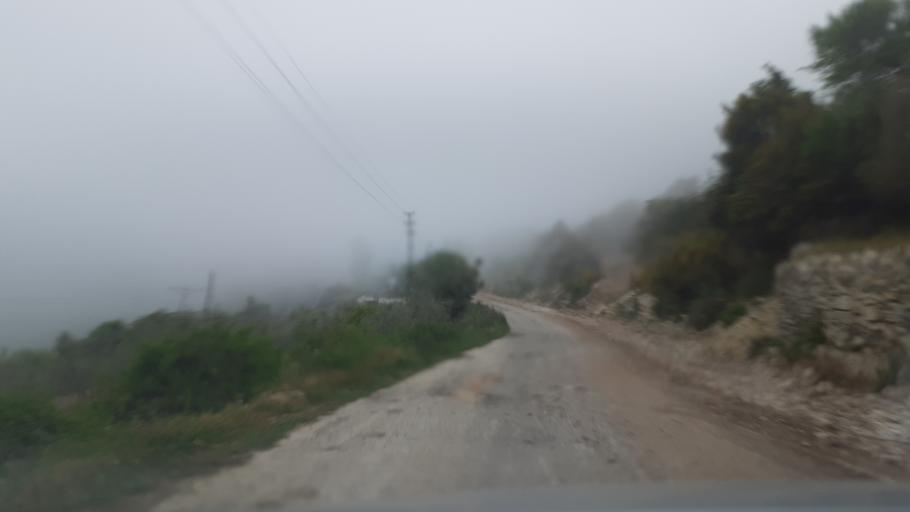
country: TR
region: Hatay
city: Yeditepe
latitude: 35.9697
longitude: 36.0048
